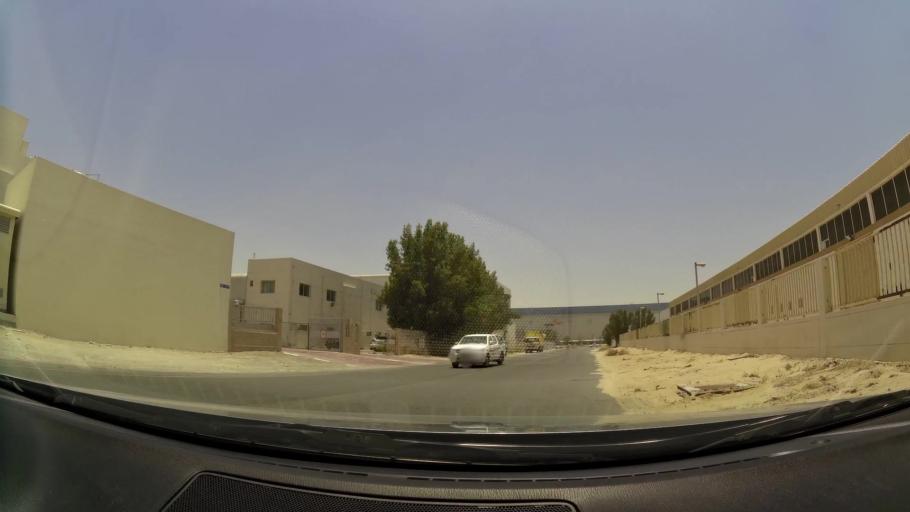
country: AE
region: Dubai
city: Dubai
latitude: 24.9844
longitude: 55.1728
